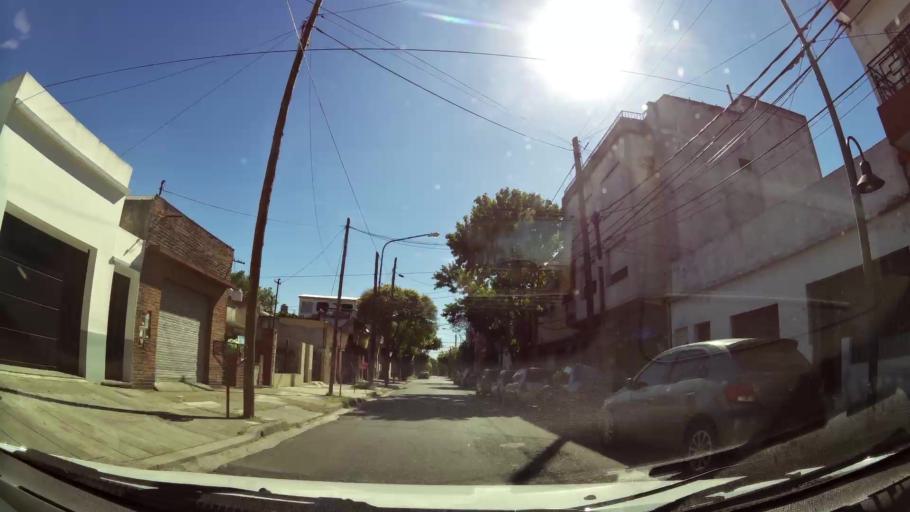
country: AR
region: Buenos Aires
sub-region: Partido de General San Martin
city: General San Martin
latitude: -34.5451
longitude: -58.5134
